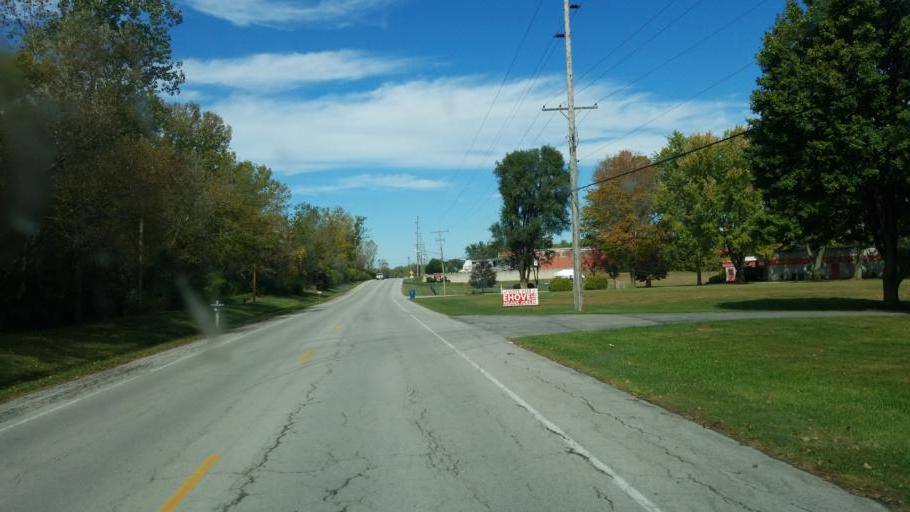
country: US
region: Ohio
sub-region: Erie County
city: Huron
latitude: 41.3767
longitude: -82.5464
